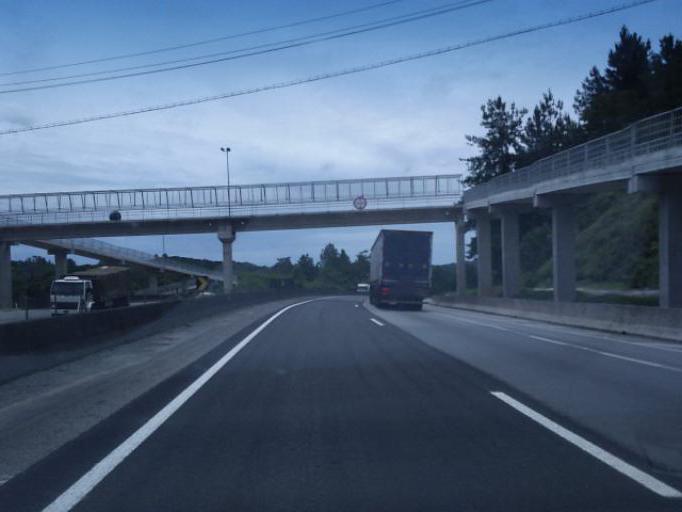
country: BR
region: Sao Paulo
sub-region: Juquitiba
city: Juquitiba
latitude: -23.9374
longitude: -47.0820
